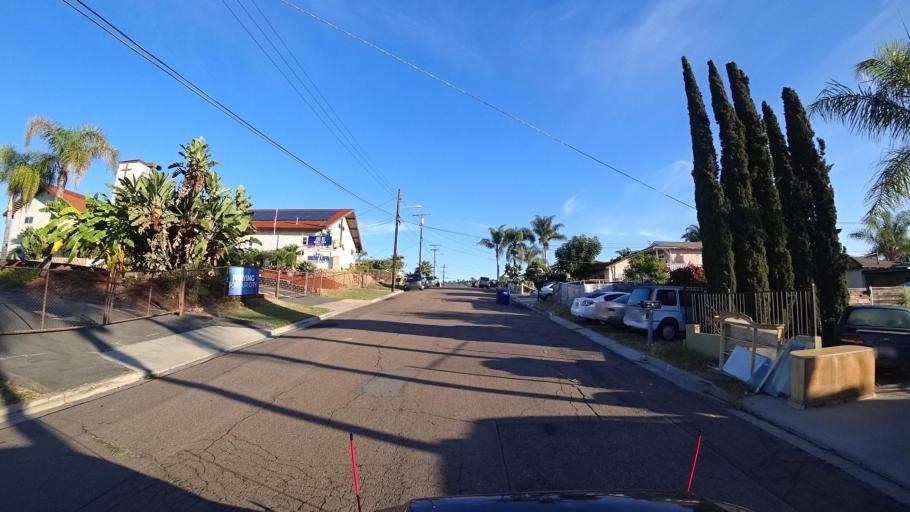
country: US
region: California
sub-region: San Diego County
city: La Presa
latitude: 32.7105
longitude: -117.0000
